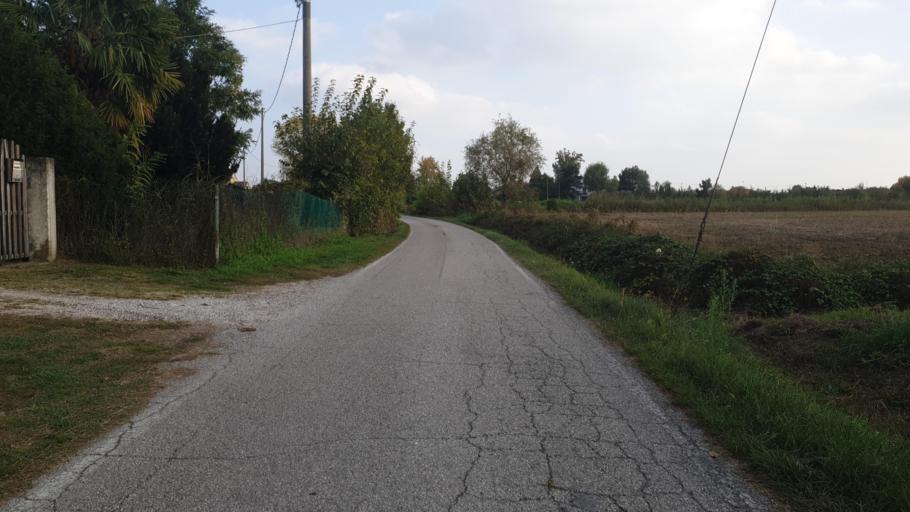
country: IT
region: Veneto
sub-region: Provincia di Padova
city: Abano Terme
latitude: 45.3437
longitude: 11.8082
